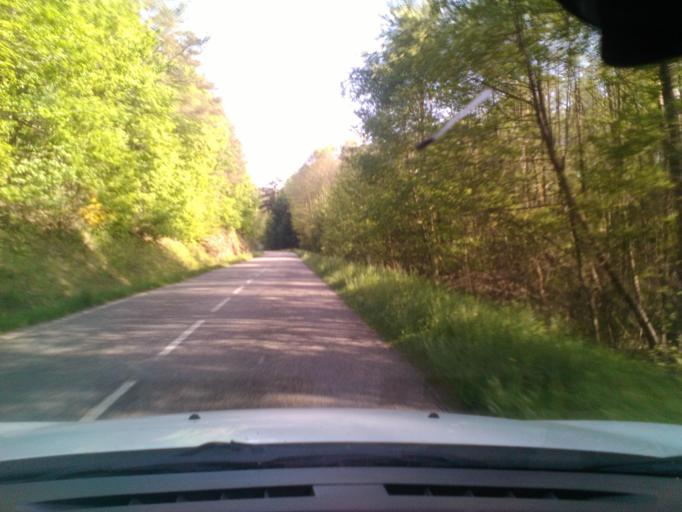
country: FR
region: Lorraine
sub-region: Departement des Vosges
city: Bruyeres
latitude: 48.2699
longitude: 6.7238
